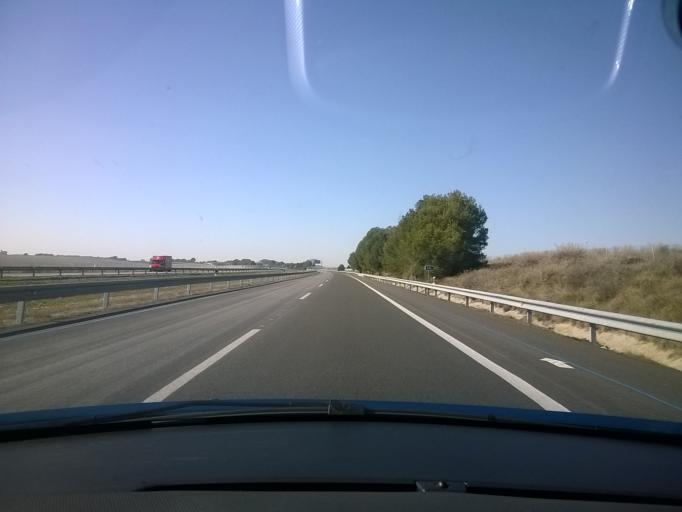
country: ES
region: Aragon
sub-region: Provincia de Zaragoza
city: Bujaraloz
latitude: 41.5214
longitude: -0.1574
